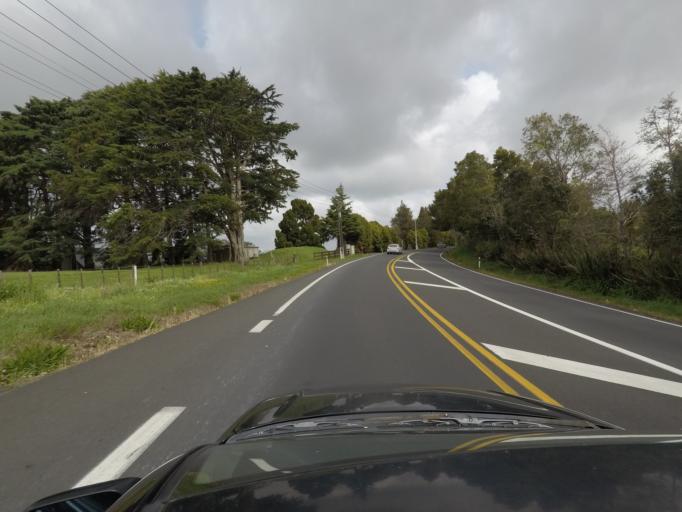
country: NZ
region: Auckland
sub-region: Auckland
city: Pakuranga
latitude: -36.9379
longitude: 174.9461
